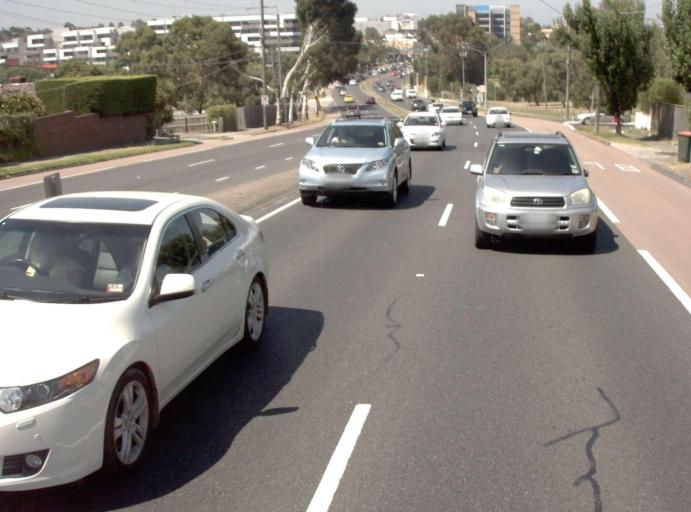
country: AU
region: Victoria
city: Ashburton
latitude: -37.8700
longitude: 145.0921
